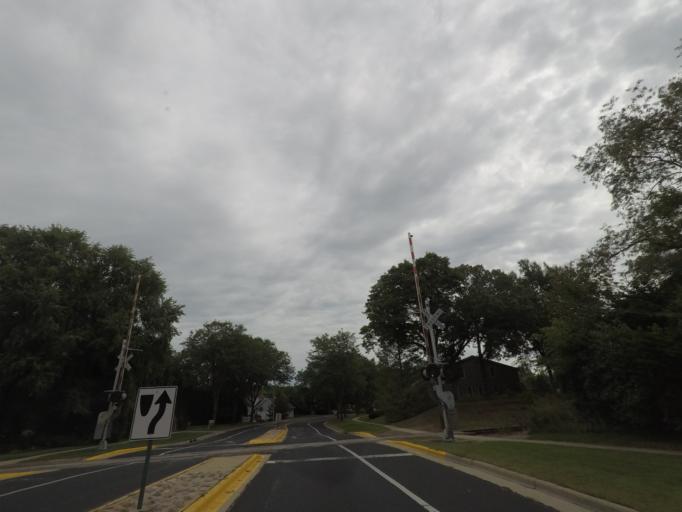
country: US
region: Wisconsin
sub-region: Dane County
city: Middleton
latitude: 43.0866
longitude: -89.4914
